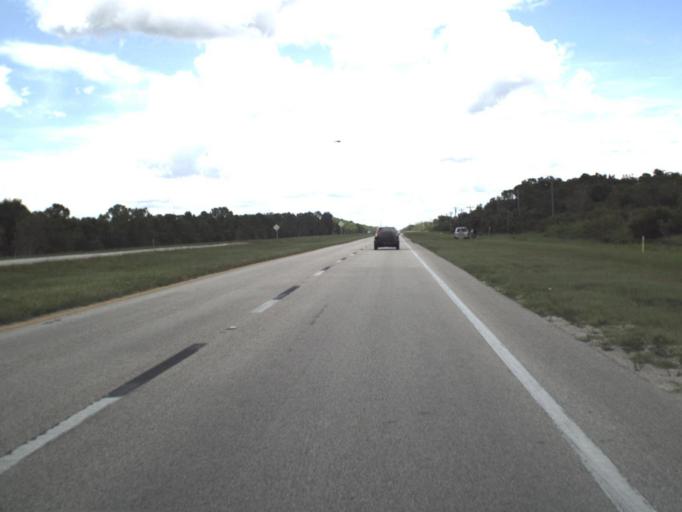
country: US
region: Florida
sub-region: Lee County
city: Suncoast Estates
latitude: 26.7885
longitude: -81.9430
